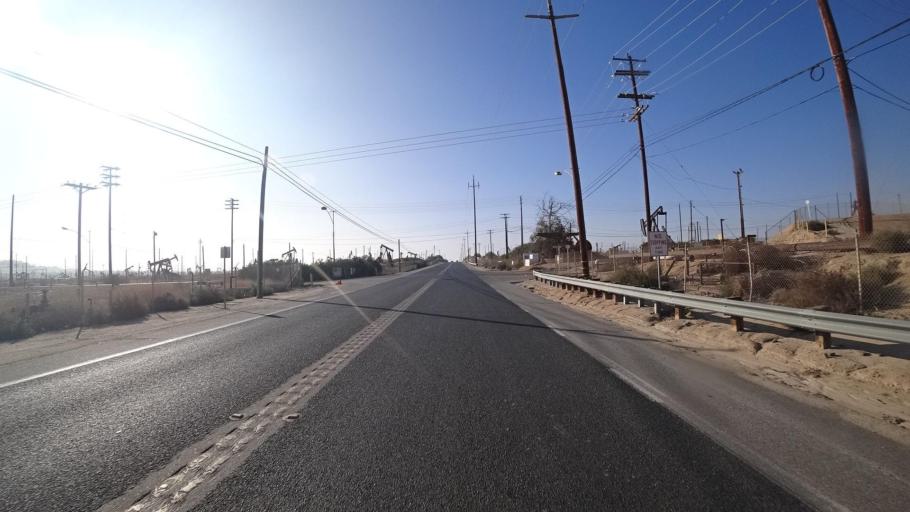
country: US
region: California
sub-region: Kern County
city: Oildale
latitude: 35.4269
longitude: -118.9807
